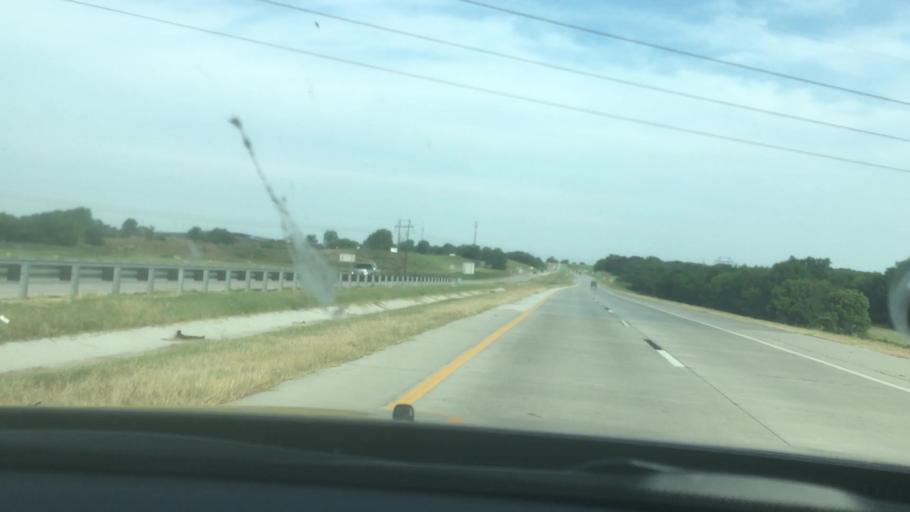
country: US
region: Oklahoma
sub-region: Pontotoc County
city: Ada
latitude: 34.7796
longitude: -96.7106
